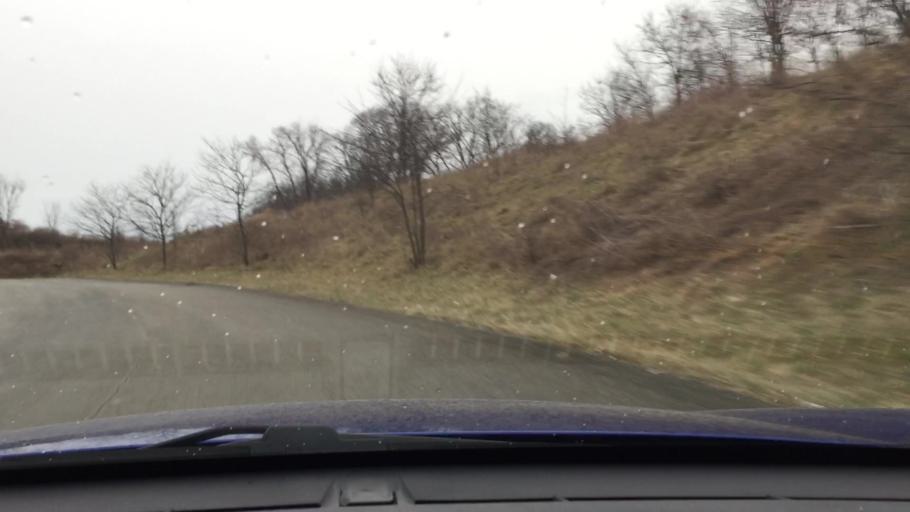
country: US
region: Pennsylvania
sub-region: Westmoreland County
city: Fellsburg
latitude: 40.1876
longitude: -79.8105
